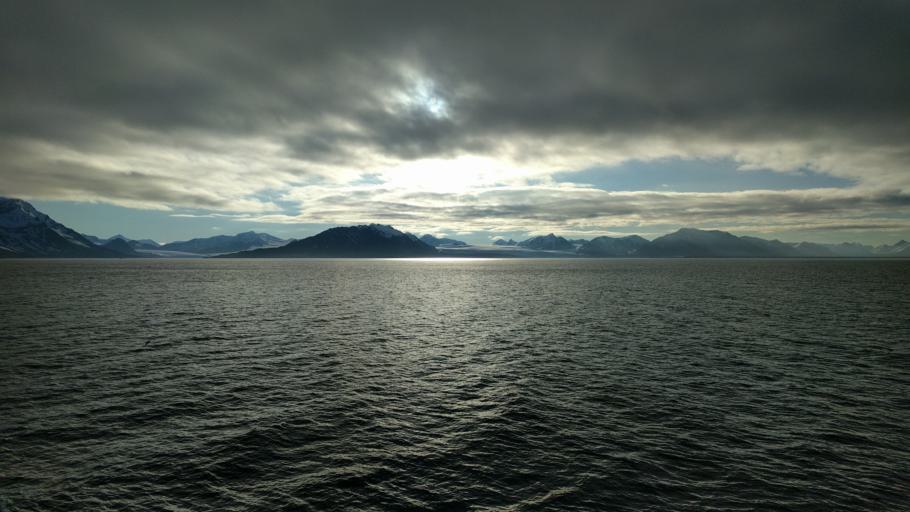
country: SJ
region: Svalbard
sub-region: Spitsbergen
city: Longyearbyen
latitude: 78.1901
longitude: 14.0893
